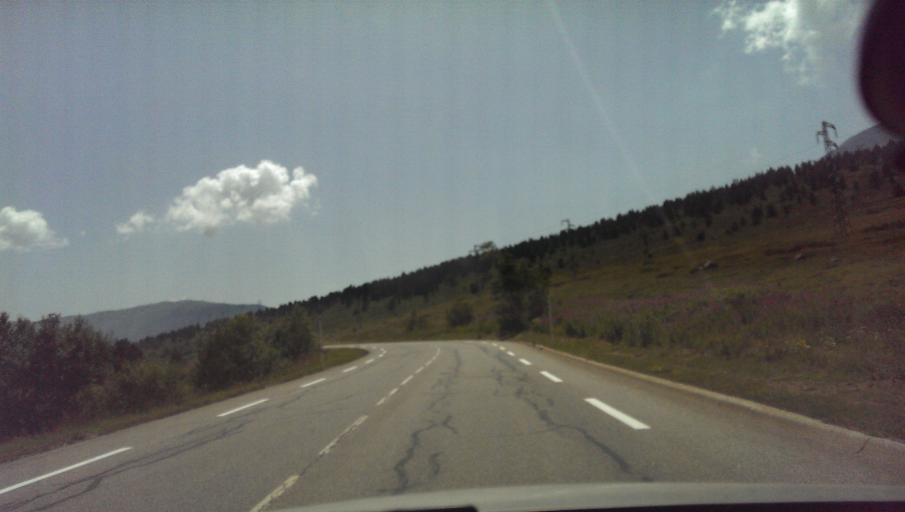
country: AD
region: Encamp
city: Pas de la Casa
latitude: 42.5651
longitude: 1.8007
